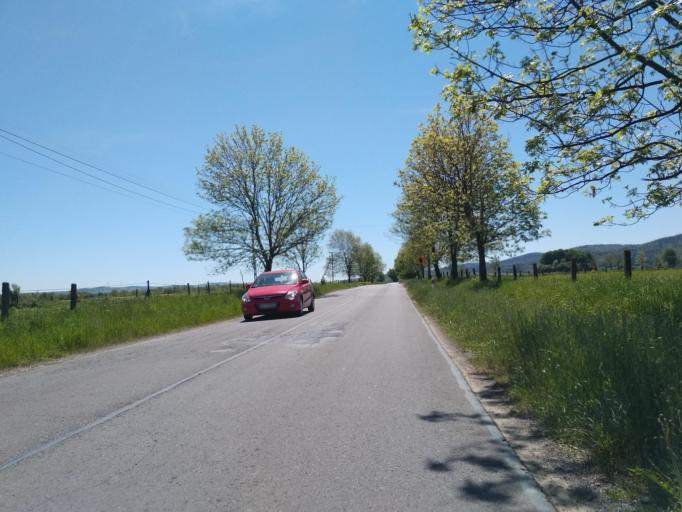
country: PL
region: Subcarpathian Voivodeship
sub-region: Powiat krosnienski
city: Sieniawa
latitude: 49.5533
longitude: 21.9381
